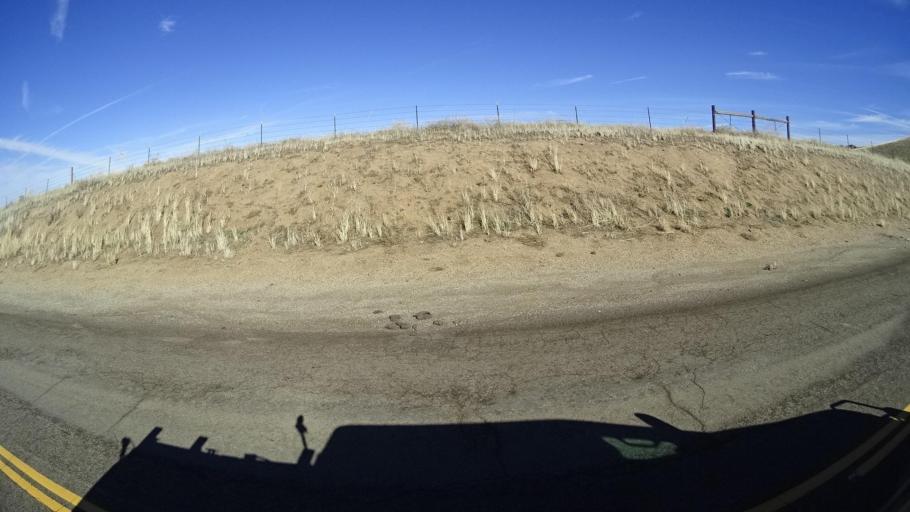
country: US
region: California
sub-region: Kern County
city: Maricopa
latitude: 34.9050
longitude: -119.3795
